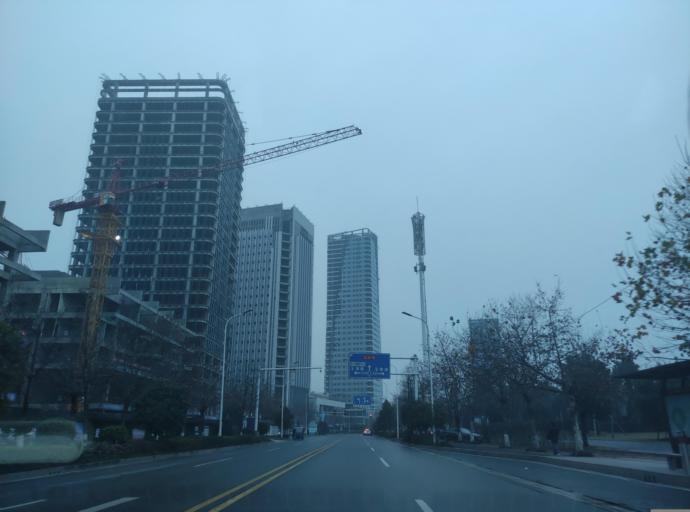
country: CN
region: Jiangxi Sheng
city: Pingxiang
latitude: 27.6661
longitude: 113.8803
